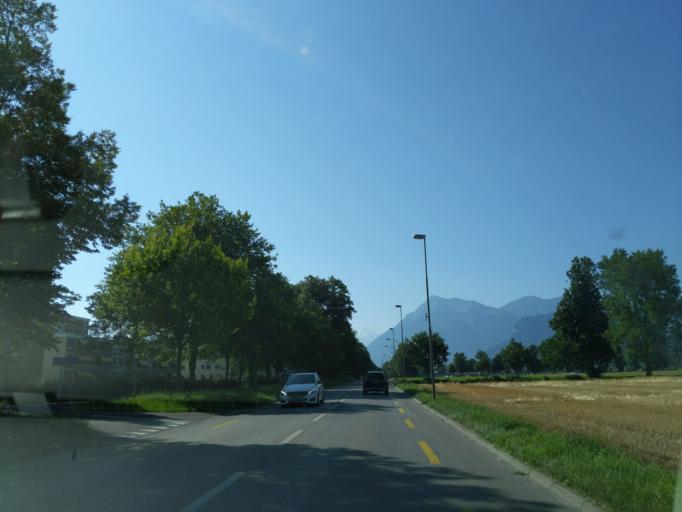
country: CH
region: Bern
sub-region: Thun District
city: Thun
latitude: 46.7517
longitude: 7.6091
